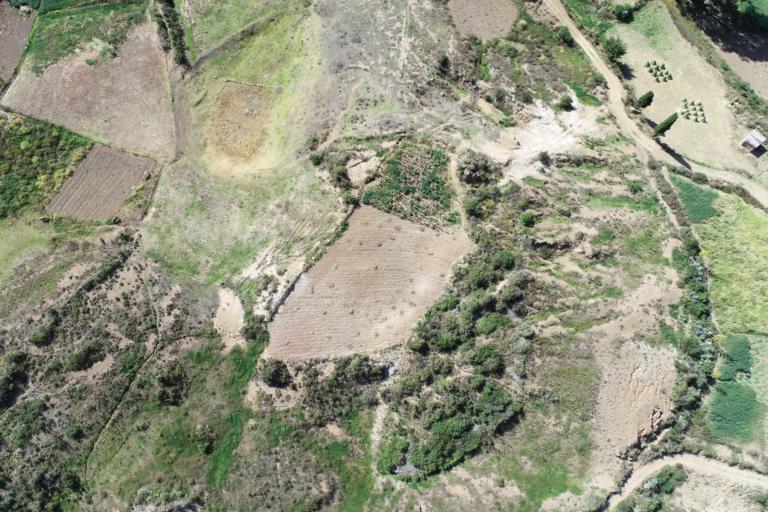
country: BO
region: La Paz
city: La Paz
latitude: -16.5566
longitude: -67.9880
